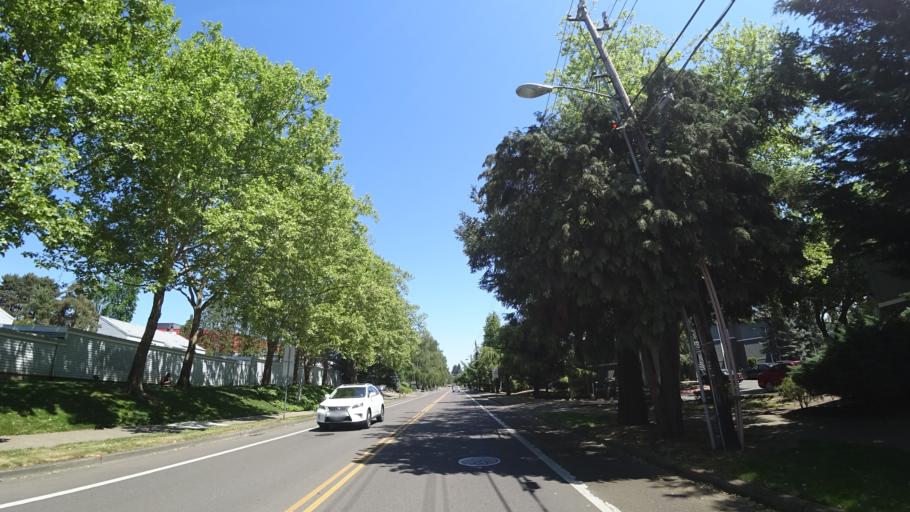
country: US
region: Oregon
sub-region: Washington County
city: Beaverton
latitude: 45.4937
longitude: -122.7964
